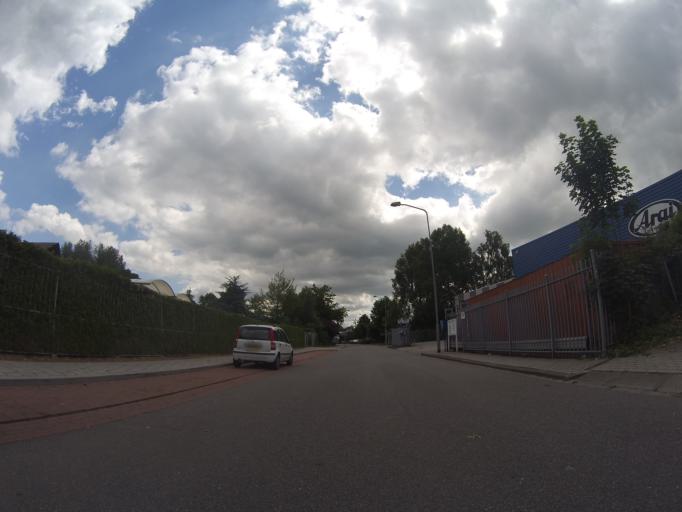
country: NL
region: Utrecht
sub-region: Gemeente Leusden
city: Leusden
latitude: 52.1689
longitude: 5.4495
